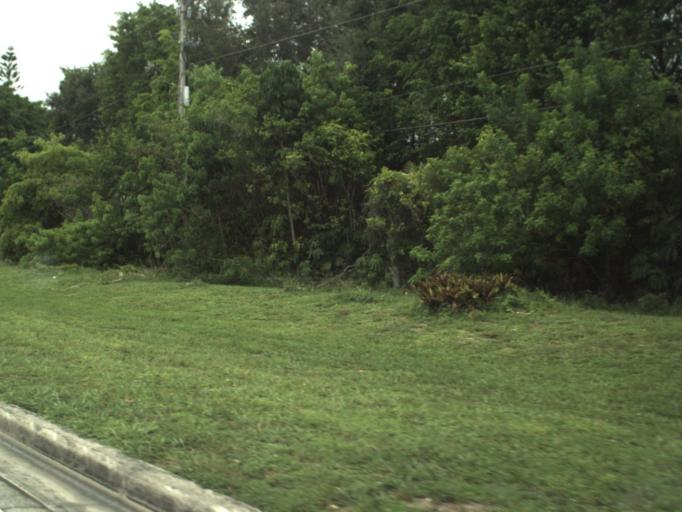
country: US
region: Florida
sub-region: Palm Beach County
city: Boca Pointe
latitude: 26.3504
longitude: -80.1678
